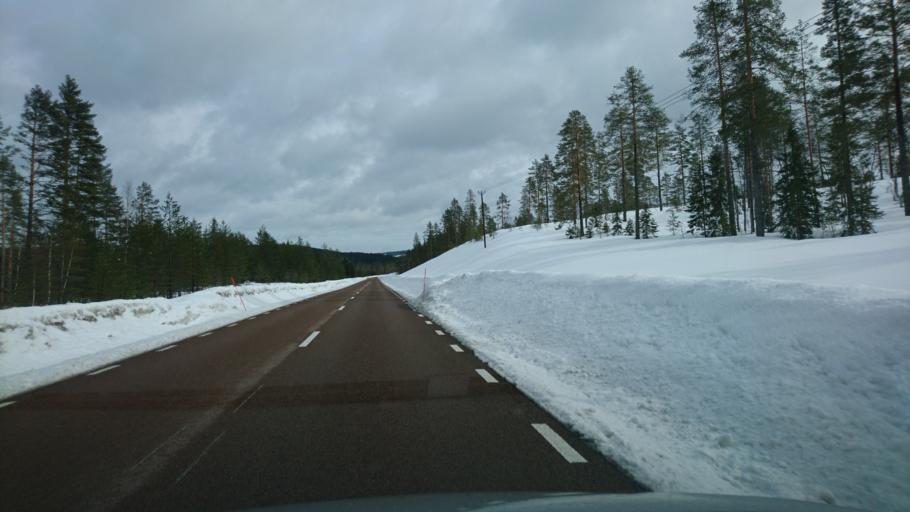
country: SE
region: Vaesternorrland
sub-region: Solleftea Kommun
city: Solleftea
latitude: 62.8571
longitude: 17.3477
